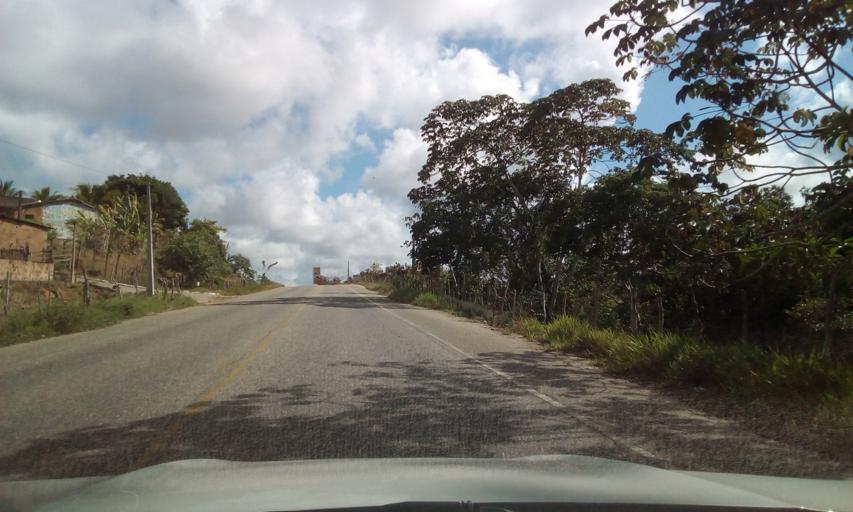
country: BR
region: Sergipe
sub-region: Estancia
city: Estancia
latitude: -11.3021
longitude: -37.4526
